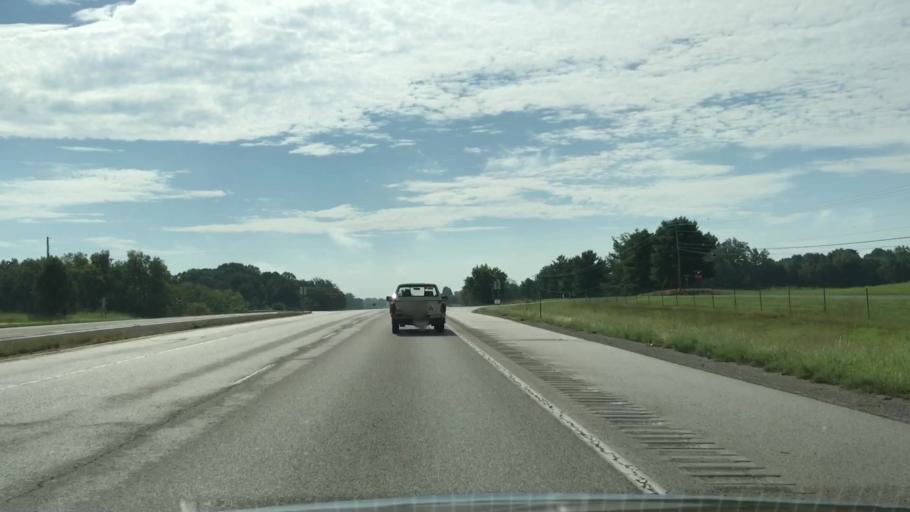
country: US
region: Kentucky
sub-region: Warren County
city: Plano
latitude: 36.8910
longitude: -86.3740
